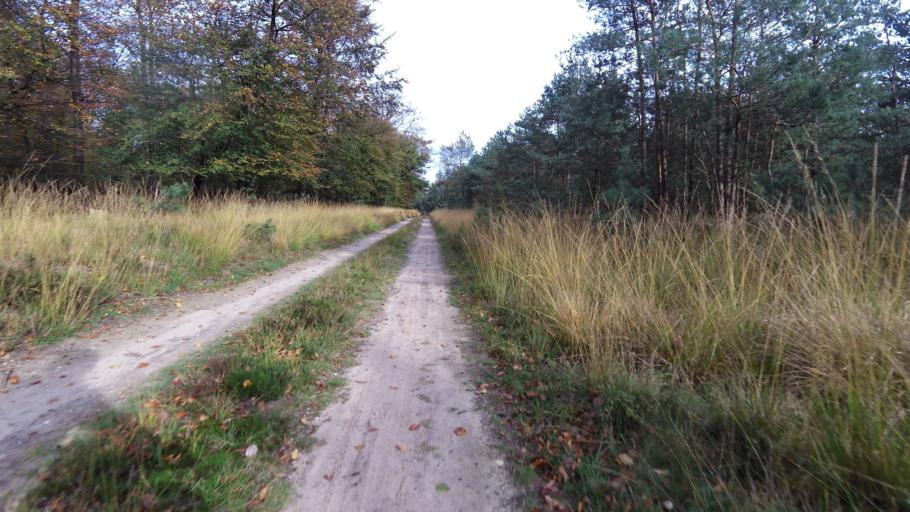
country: NL
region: Gelderland
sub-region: Gemeente Apeldoorn
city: Uddel
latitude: 52.3098
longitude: 5.8523
